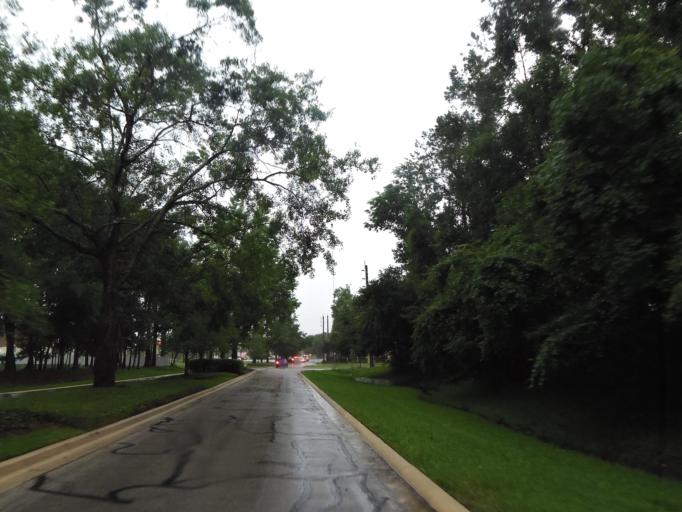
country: US
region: Florida
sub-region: Duval County
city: Jacksonville
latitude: 30.2889
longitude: -81.5641
